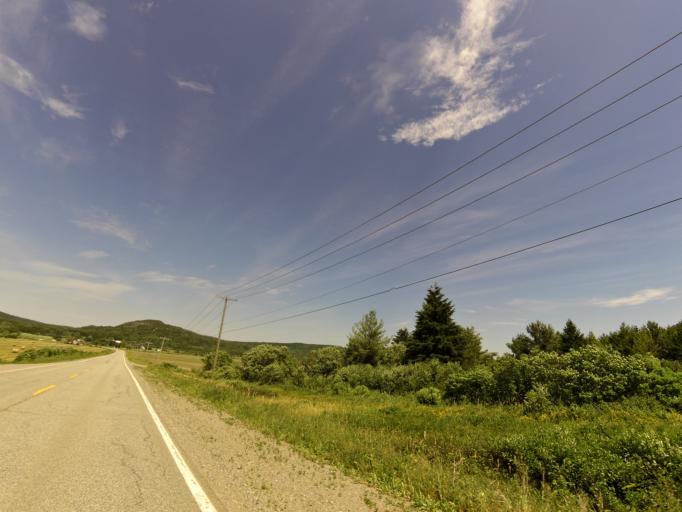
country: CA
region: Quebec
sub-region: Abitibi-Temiscamingue
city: Ville-Marie
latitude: 47.2749
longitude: -79.4107
